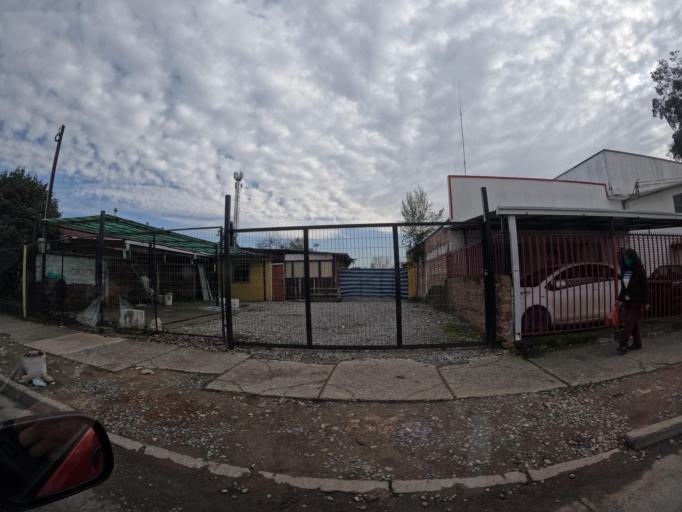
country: CL
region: Maule
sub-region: Provincia de Linares
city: Linares
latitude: -35.8518
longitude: -71.5852
